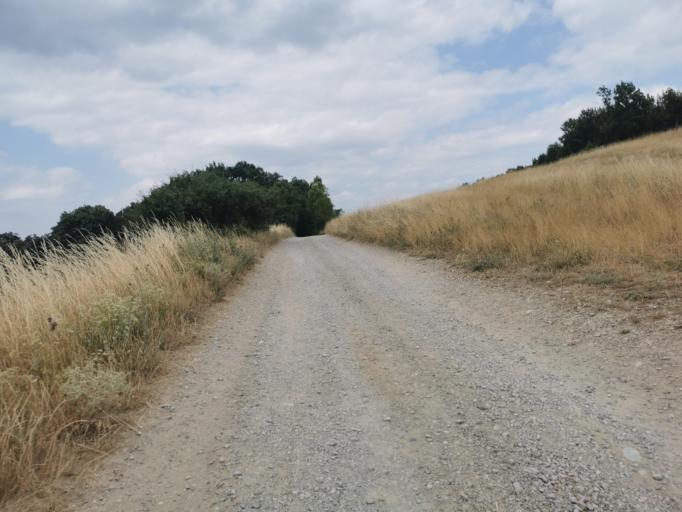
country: SK
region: Nitriansky
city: Brezova pod Bradlom
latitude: 48.6841
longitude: 17.5043
